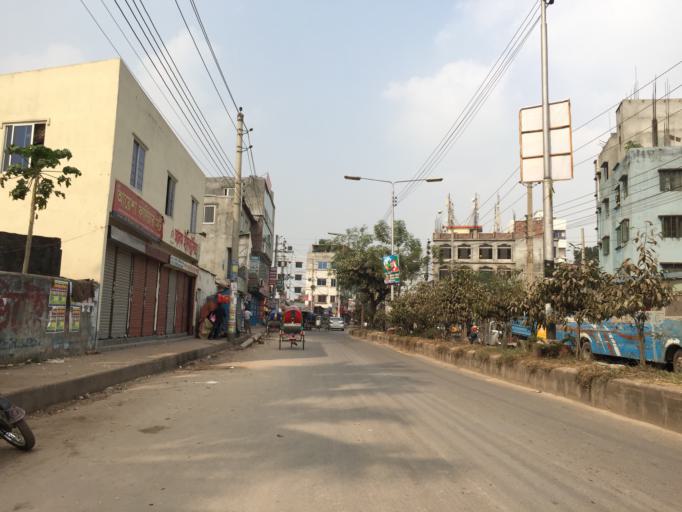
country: BD
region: Dhaka
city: Azimpur
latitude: 23.7883
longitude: 90.3667
